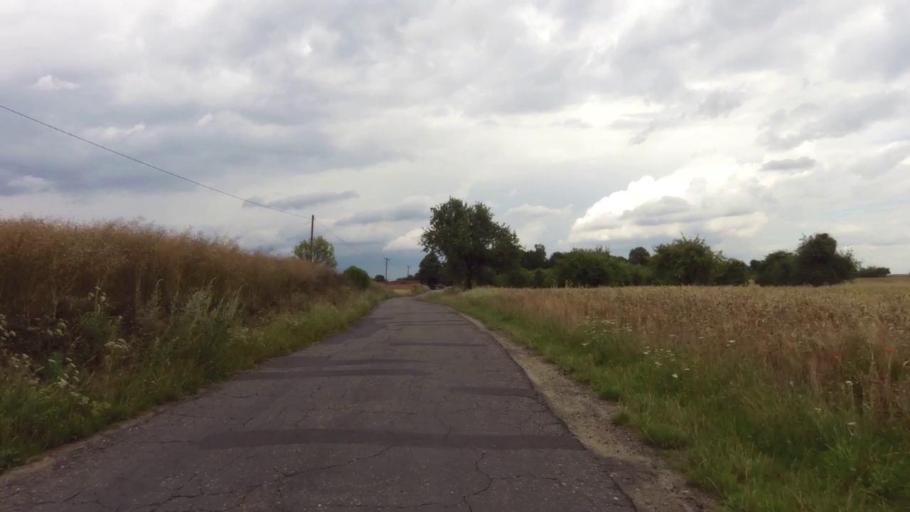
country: PL
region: West Pomeranian Voivodeship
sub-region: Powiat gryfinski
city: Moryn
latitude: 52.8943
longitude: 14.4110
